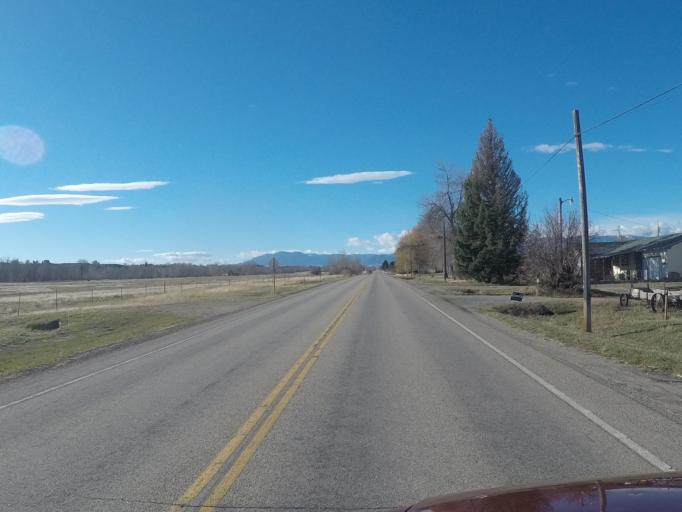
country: US
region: Montana
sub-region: Carbon County
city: Red Lodge
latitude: 45.3564
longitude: -109.1702
